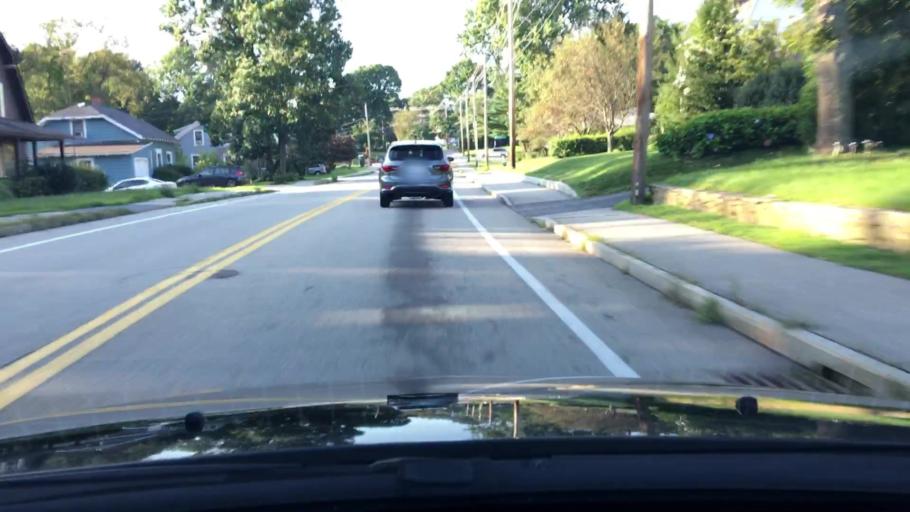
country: US
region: Massachusetts
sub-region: Worcester County
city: Shrewsbury
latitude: 42.2896
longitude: -71.7119
